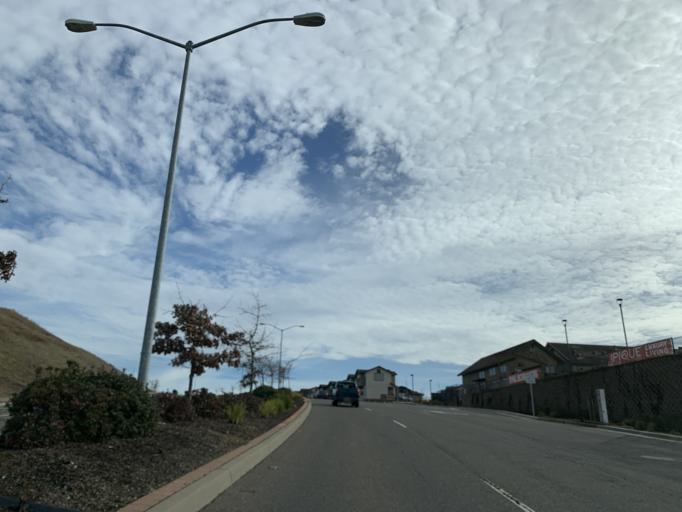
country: US
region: California
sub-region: El Dorado County
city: El Dorado Hills
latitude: 38.6467
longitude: -121.1003
